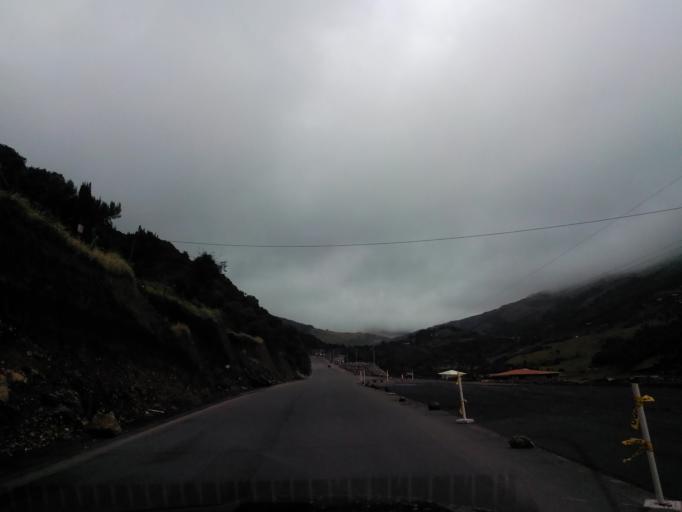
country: EC
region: Pichincha
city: Sangolqui
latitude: -0.3774
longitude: -78.1875
